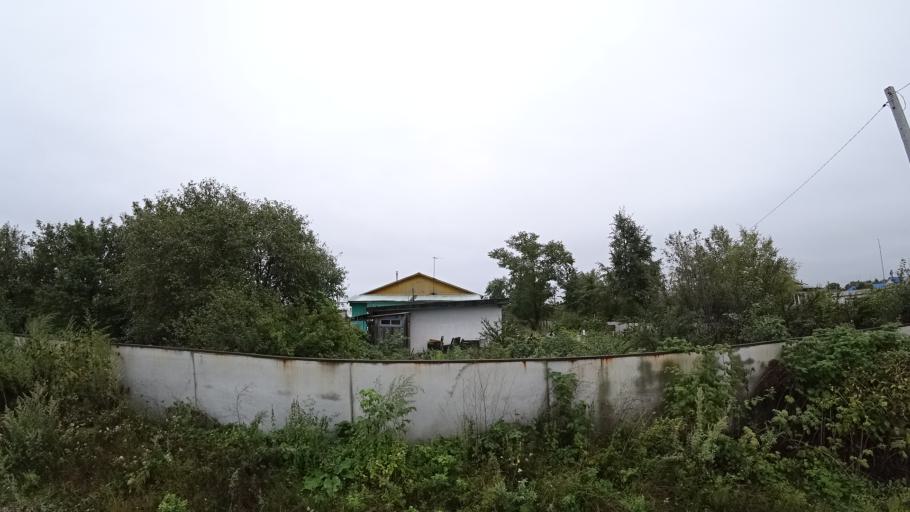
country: RU
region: Primorskiy
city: Monastyrishche
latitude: 44.2045
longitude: 132.4268
